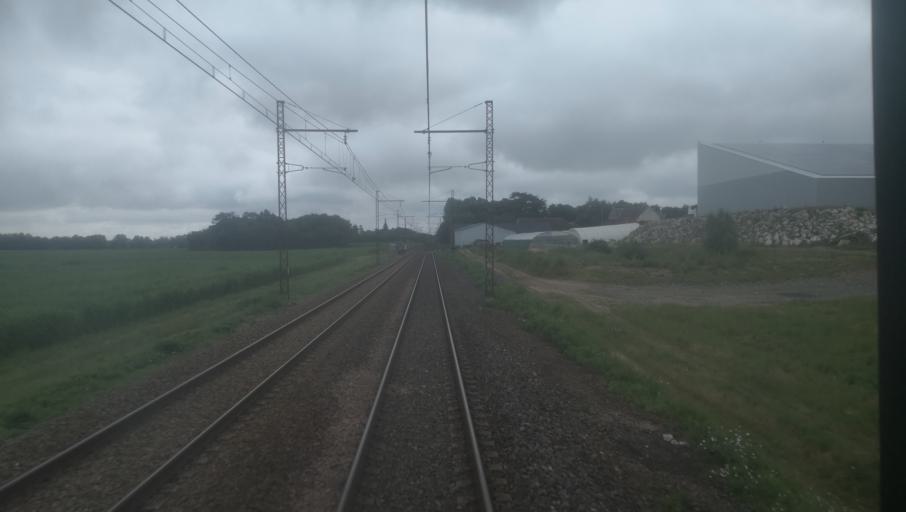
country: FR
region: Centre
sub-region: Departement du Cher
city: Mereau
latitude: 47.1418
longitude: 2.0482
